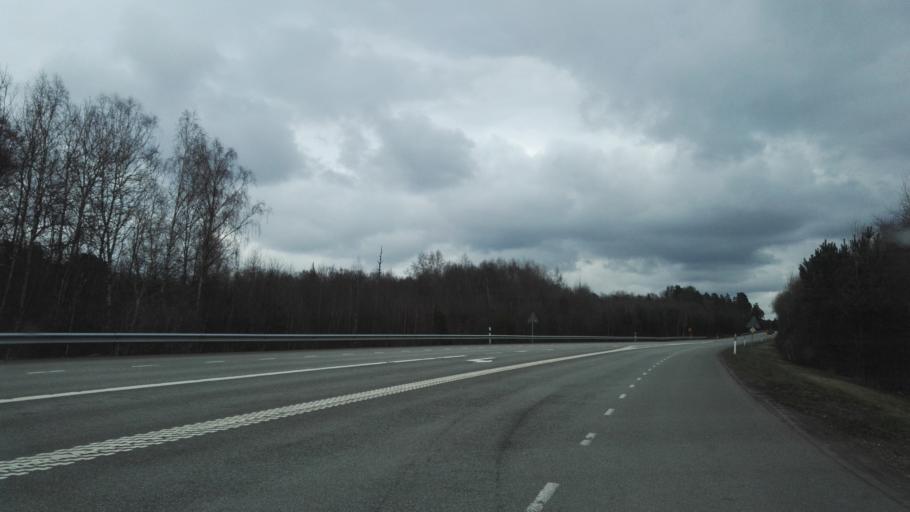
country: SE
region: Skane
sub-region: Hassleholms Kommun
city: Hassleholm
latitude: 56.1714
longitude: 13.8207
